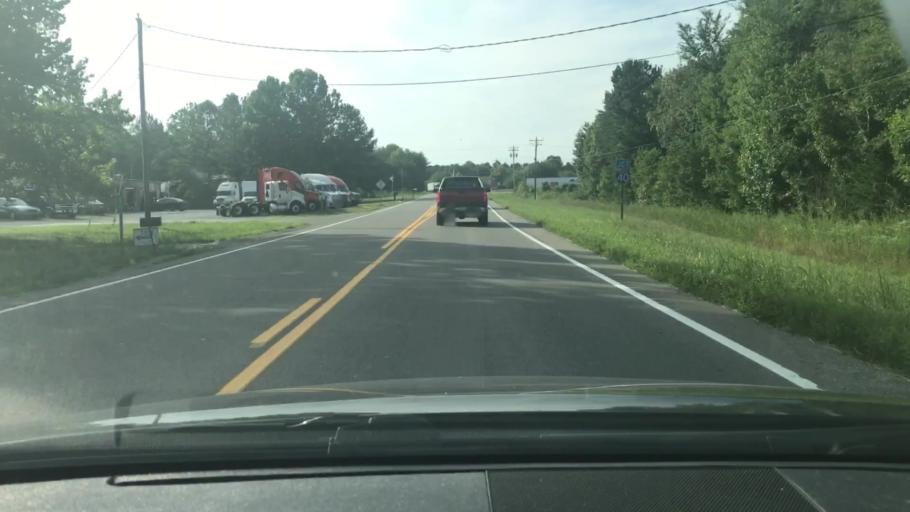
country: US
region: Tennessee
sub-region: Williamson County
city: Fairview
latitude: 36.0242
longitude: -87.1701
